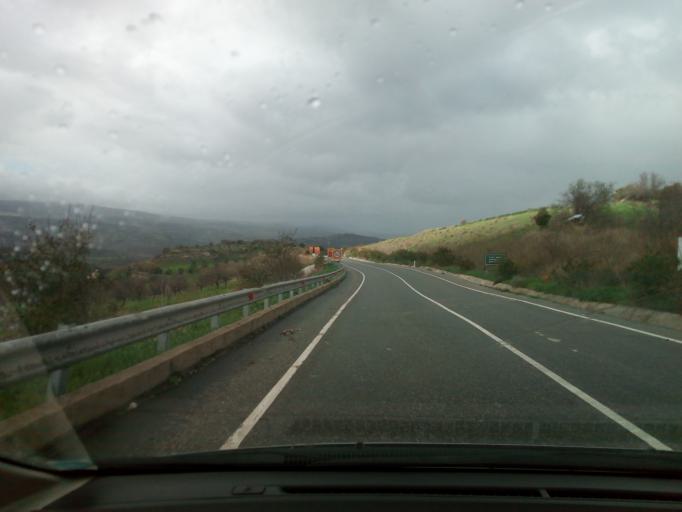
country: CY
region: Pafos
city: Polis
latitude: 34.9454
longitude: 32.4998
